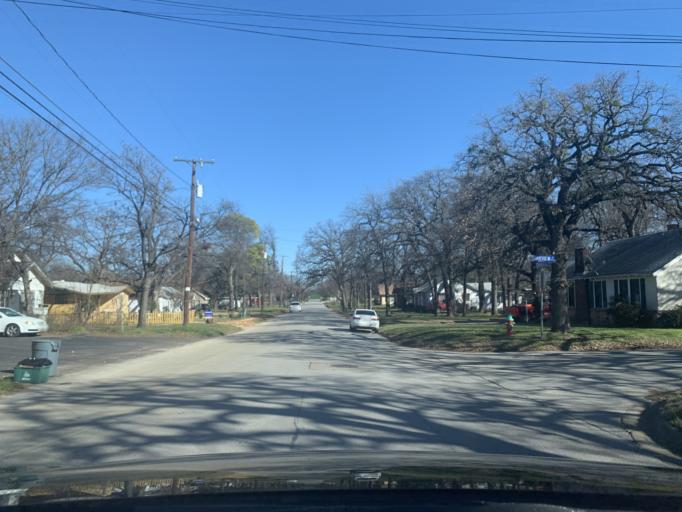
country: US
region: Texas
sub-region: Tarrant County
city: Haltom City
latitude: 32.7817
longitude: -97.2798
